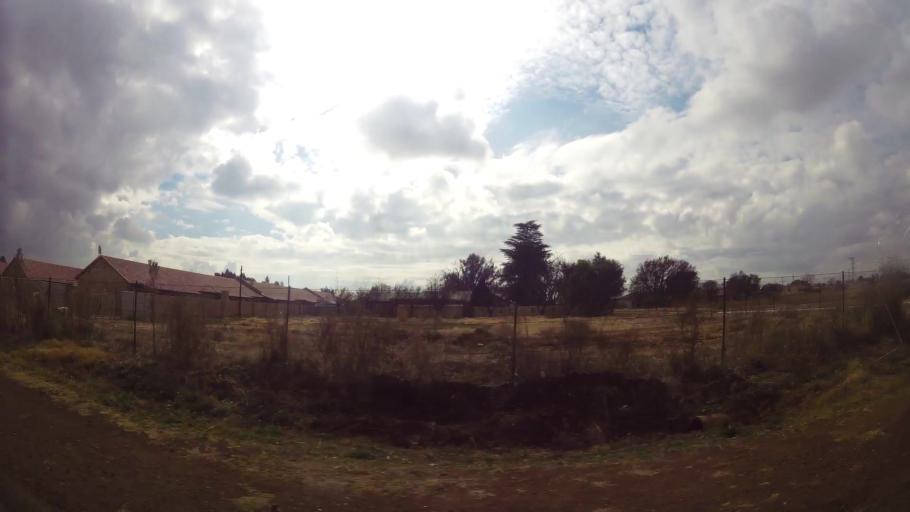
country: ZA
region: Gauteng
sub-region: Sedibeng District Municipality
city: Meyerton
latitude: -26.5982
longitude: 28.0342
